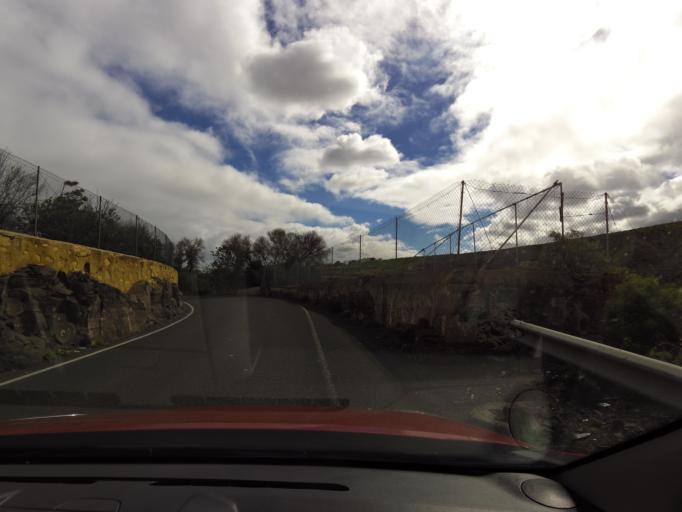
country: ES
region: Canary Islands
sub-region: Provincia de Las Palmas
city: Telde
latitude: 28.0079
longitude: -15.4280
